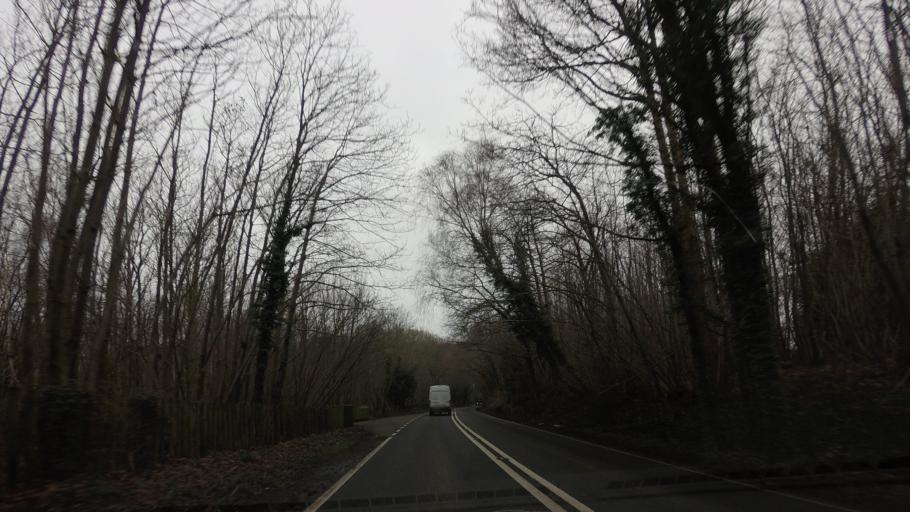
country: GB
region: England
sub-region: Kent
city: Staplehurst
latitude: 51.1276
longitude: 0.5610
